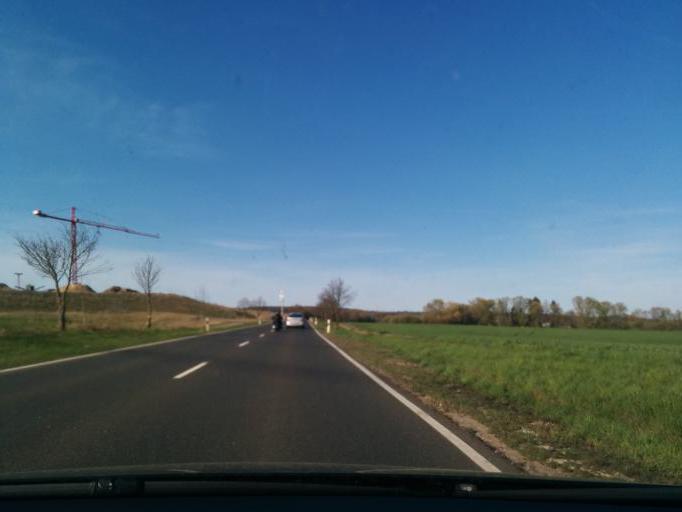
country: DE
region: Rheinland-Pfalz
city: Windesheim
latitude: 49.9166
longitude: 7.8204
